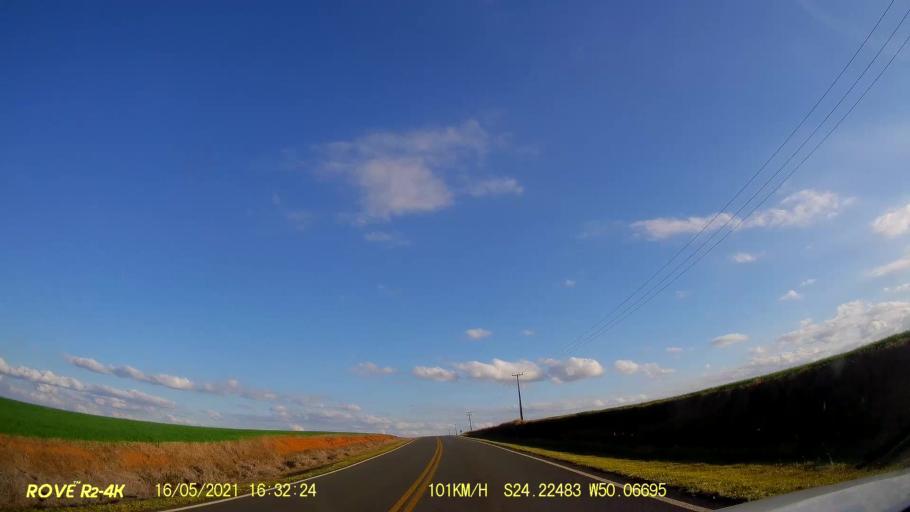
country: BR
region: Parana
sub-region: Pirai Do Sul
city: Pirai do Sul
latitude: -24.2243
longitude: -50.0661
